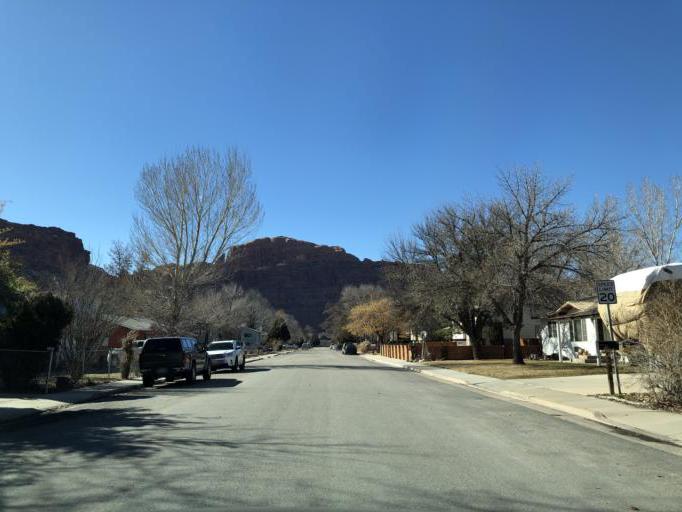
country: US
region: Utah
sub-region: Grand County
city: Moab
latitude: 38.5755
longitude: -109.5618
